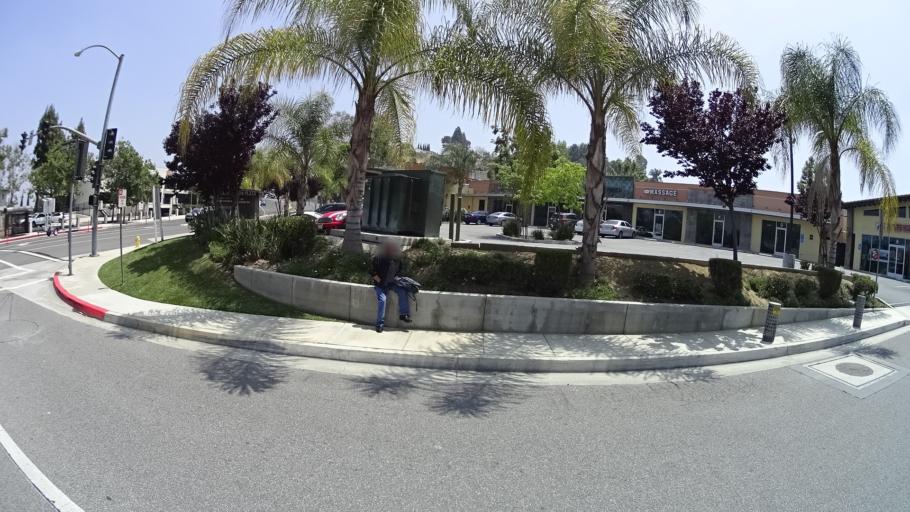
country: US
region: California
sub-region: Los Angeles County
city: Belvedere
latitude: 34.0620
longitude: -118.1529
